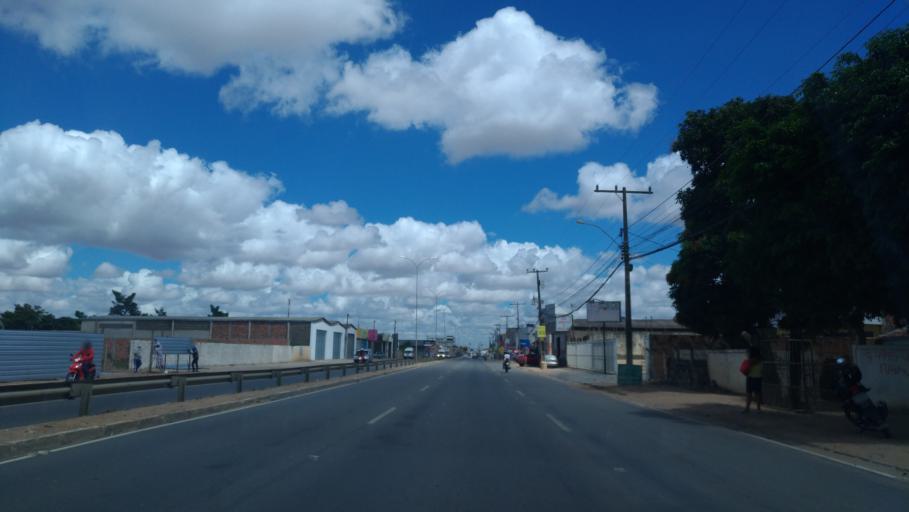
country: BR
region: Alagoas
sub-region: Arapiraca
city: Arapiraca
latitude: -9.7286
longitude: -36.6660
